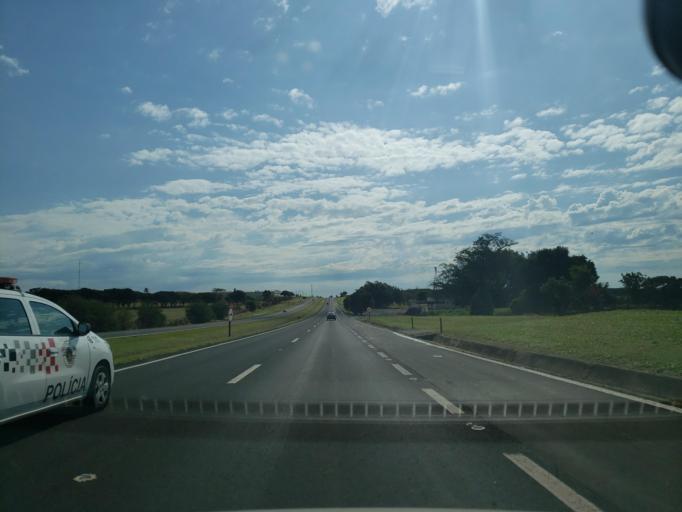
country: BR
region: Sao Paulo
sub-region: Pirajui
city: Pirajui
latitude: -22.0102
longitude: -49.4216
